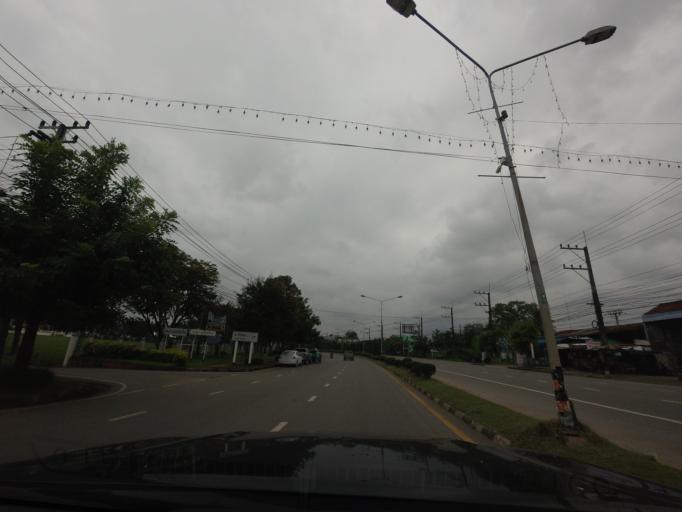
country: TH
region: Nong Khai
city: Si Chiang Mai
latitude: 17.9572
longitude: 102.5905
